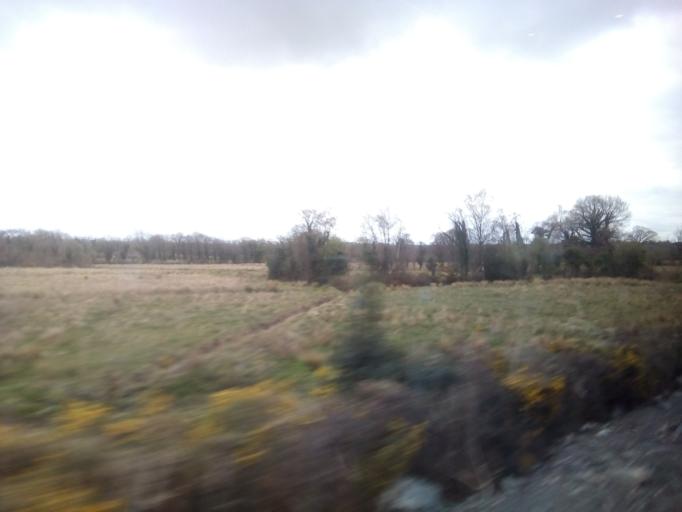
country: IE
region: Leinster
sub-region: An Longfort
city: Longford
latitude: 53.7954
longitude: -7.8492
